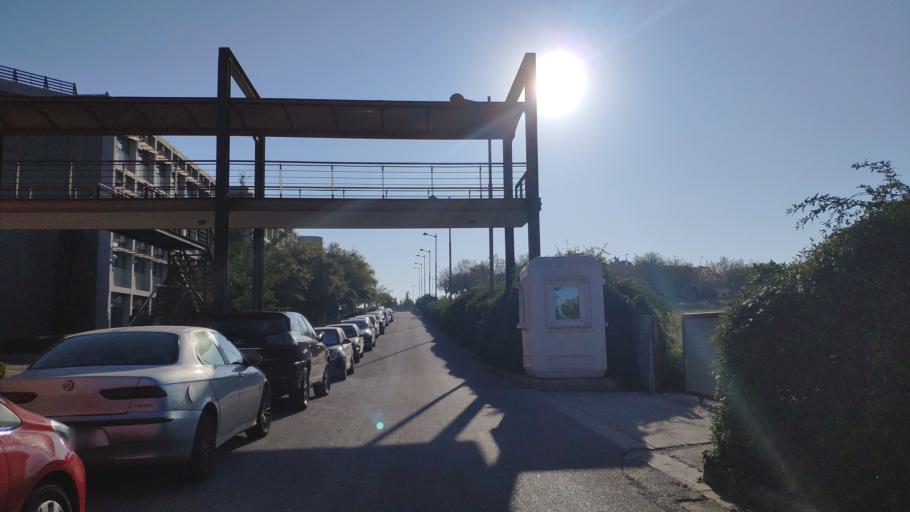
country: GR
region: Thessaly
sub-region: Nomos Larisis
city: Terpsithea
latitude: 39.6142
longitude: 22.3870
